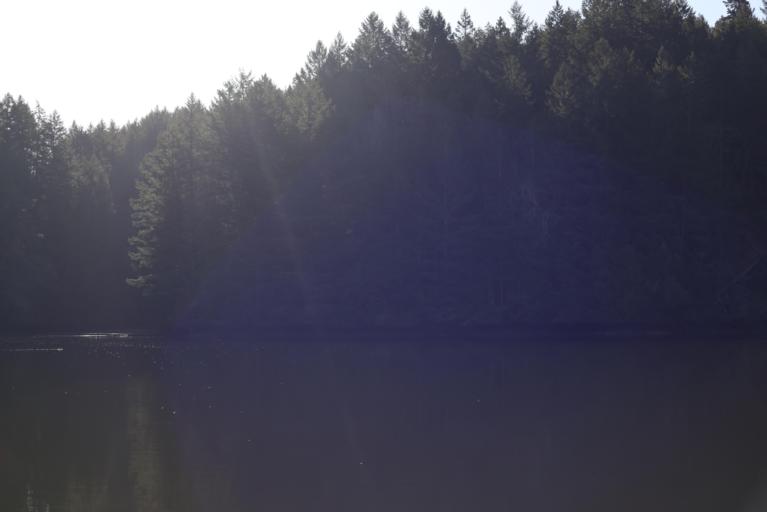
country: CA
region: British Columbia
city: Langford
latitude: 48.5596
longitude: -123.4670
